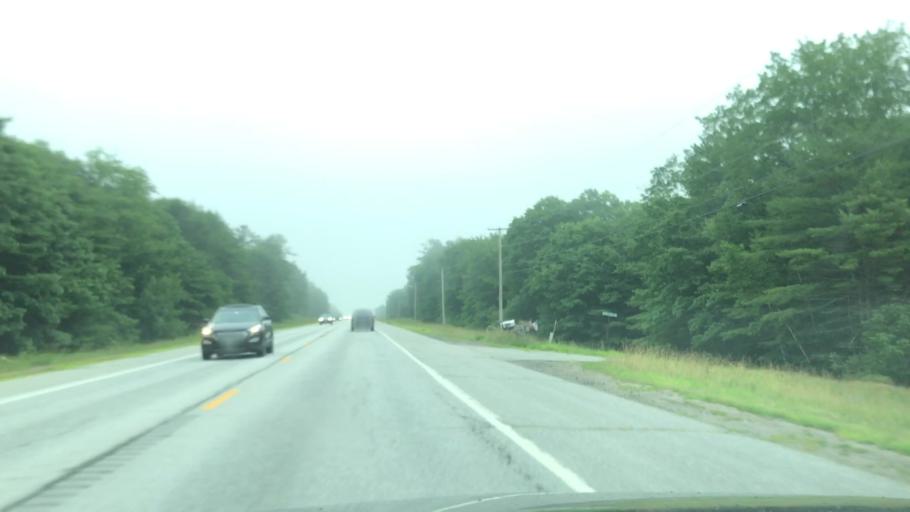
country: US
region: Maine
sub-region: Lincoln County
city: Nobleboro
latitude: 44.0820
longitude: -69.4742
